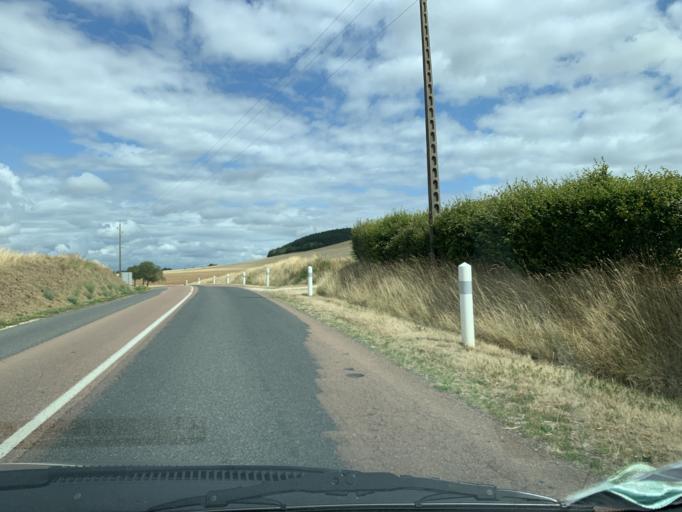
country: FR
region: Bourgogne
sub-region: Departement de la Nievre
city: Varzy
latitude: 47.3636
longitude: 3.4075
